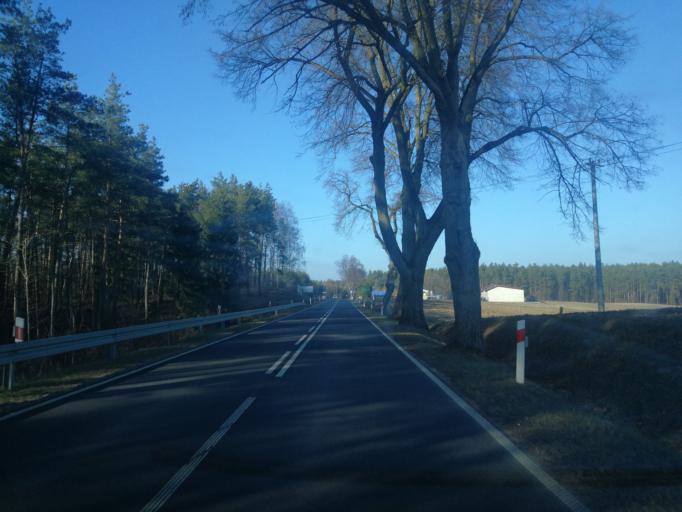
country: PL
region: Warmian-Masurian Voivodeship
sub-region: Powiat dzialdowski
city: Lidzbark
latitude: 53.3035
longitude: 19.8130
